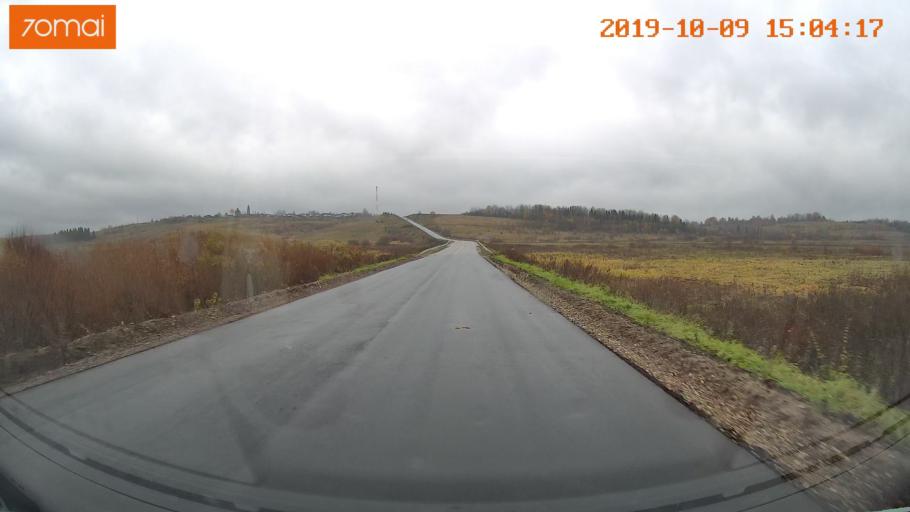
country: RU
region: Kostroma
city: Chistyye Bory
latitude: 58.2605
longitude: 41.6686
